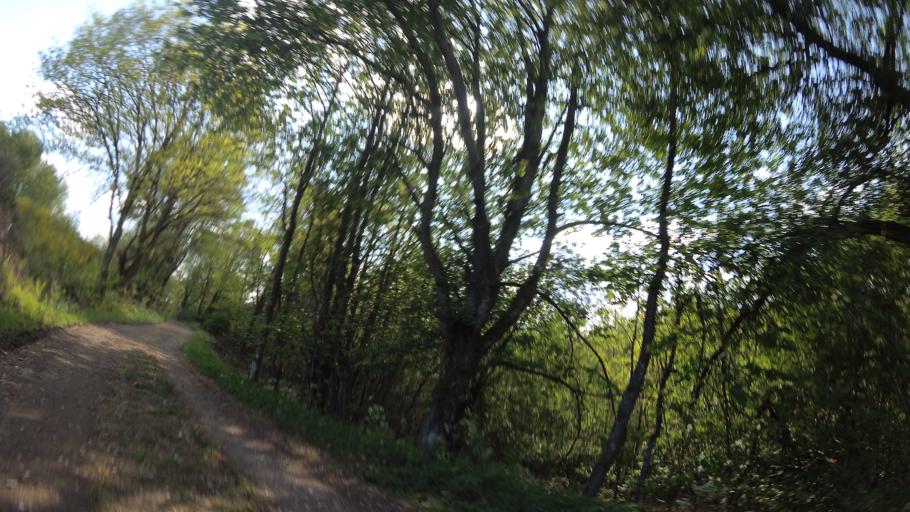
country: DE
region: Rheinland-Pfalz
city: Herchweiler
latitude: 49.4965
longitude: 7.2457
